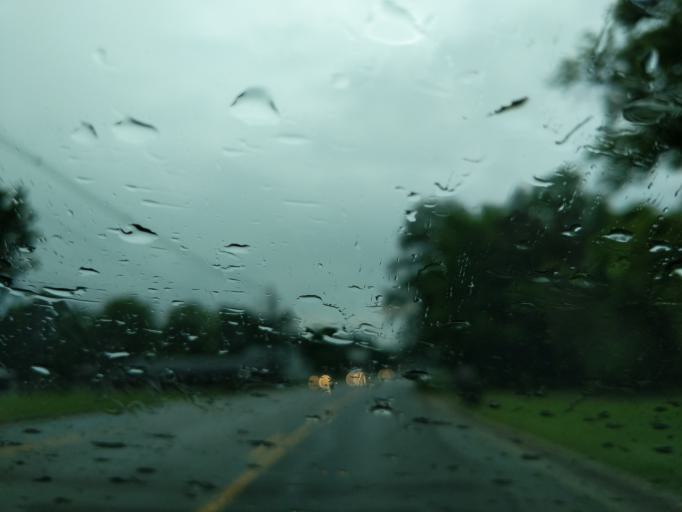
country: US
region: Indiana
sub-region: Madison County
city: Chesterfield
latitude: 40.0895
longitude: -85.6365
